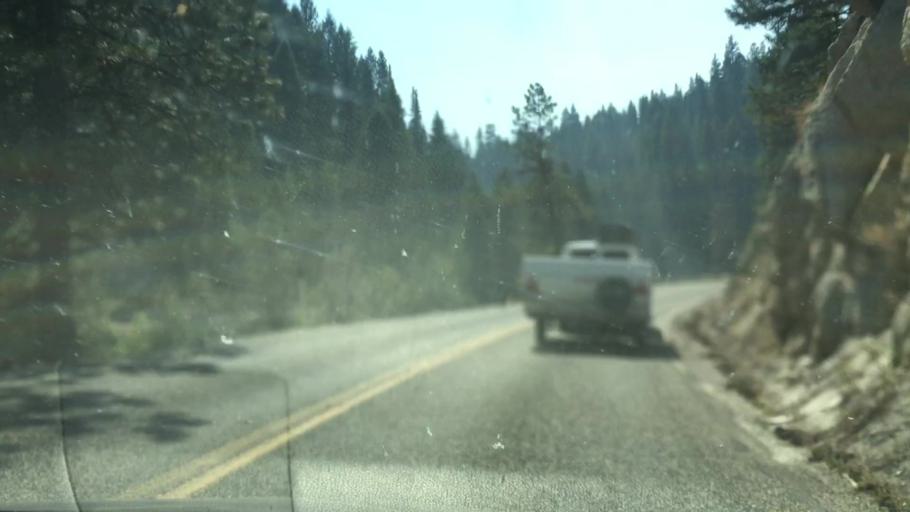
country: US
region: Idaho
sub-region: Valley County
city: Cascade
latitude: 44.3177
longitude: -116.0643
